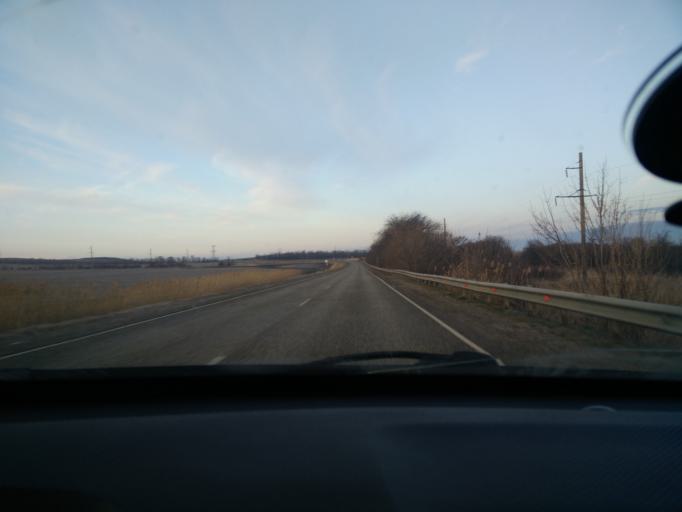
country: RU
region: Stavropol'skiy
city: Balakhonovskoye
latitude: 44.9944
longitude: 41.7226
